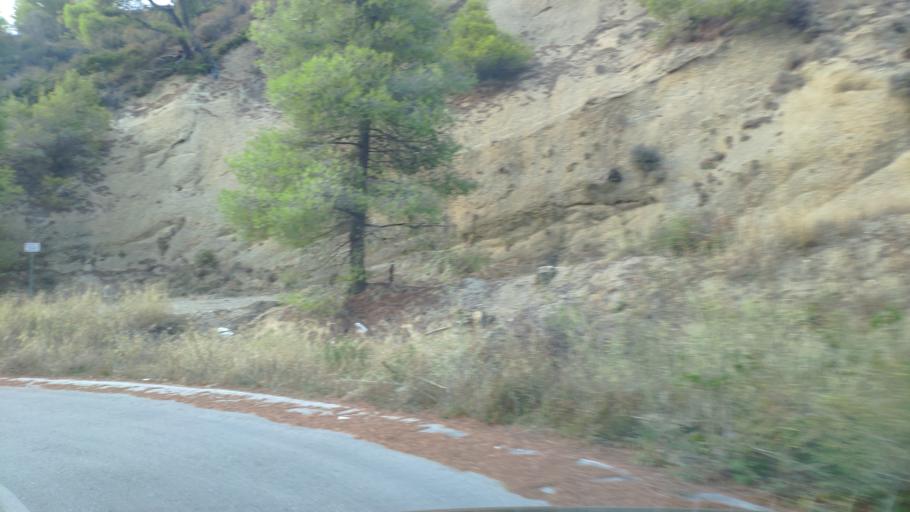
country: GR
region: West Greece
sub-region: Nomos Achaias
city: Aiyira
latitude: 38.1001
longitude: 22.4052
